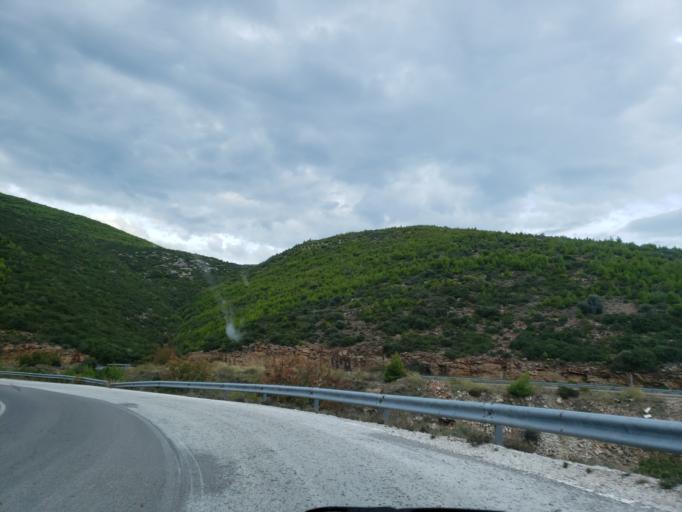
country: GR
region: Attica
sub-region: Nomarchia Anatolikis Attikis
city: Grammatiko
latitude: 38.2104
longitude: 23.9461
